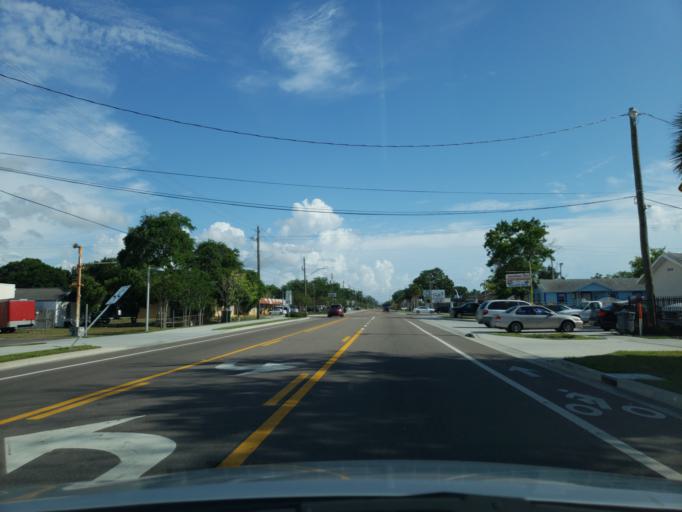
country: US
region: Florida
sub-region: Hillsborough County
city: Egypt Lake-Leto
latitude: 27.9872
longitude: -82.5136
